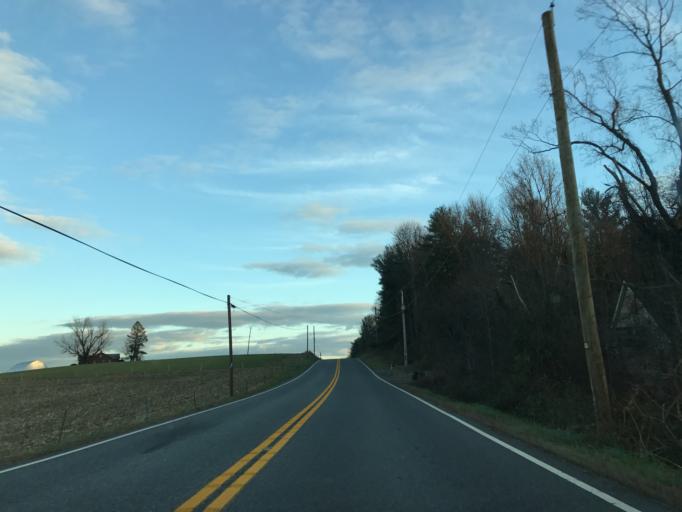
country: US
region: Pennsylvania
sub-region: York County
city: Susquehanna Trails
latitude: 39.7058
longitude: -76.2565
